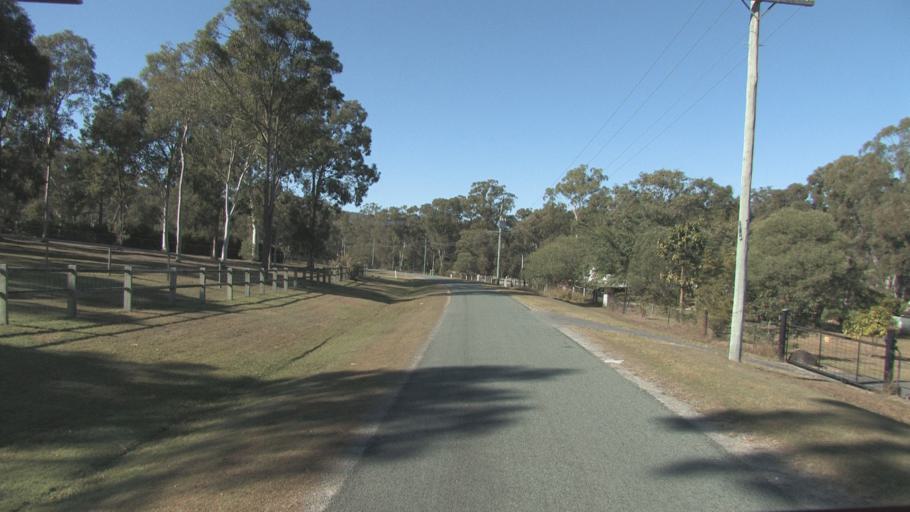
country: AU
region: Queensland
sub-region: Logan
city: Chambers Flat
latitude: -27.7731
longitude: 153.1252
